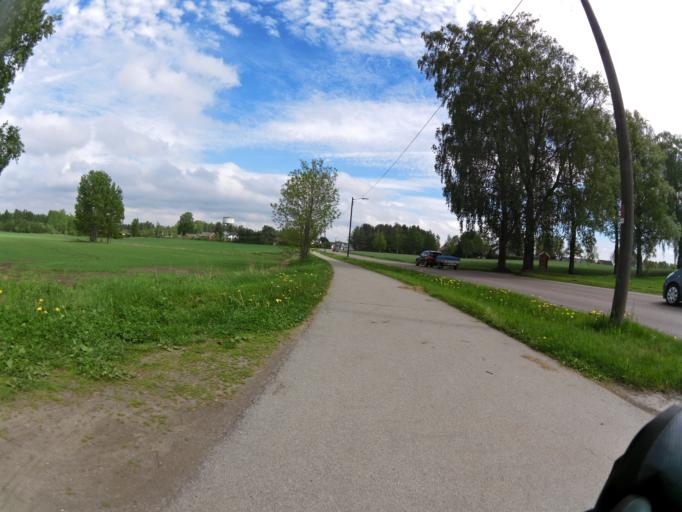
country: NO
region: Ostfold
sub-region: Rade
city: Karlshus
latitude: 59.3491
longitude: 10.8831
